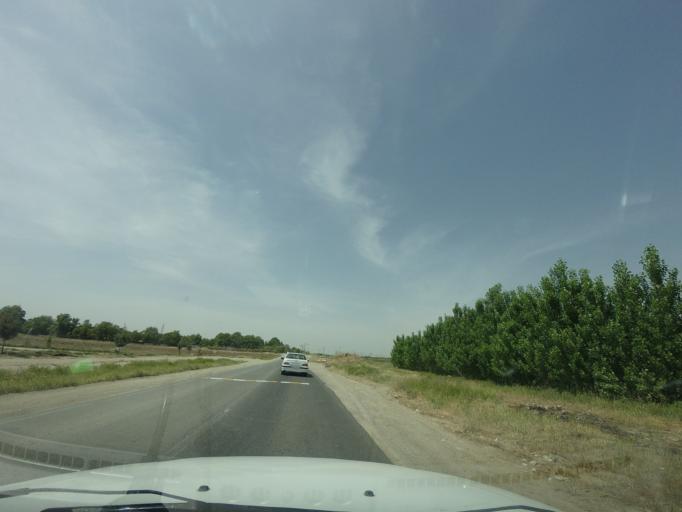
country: IR
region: Tehran
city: Eslamshahr
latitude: 35.6414
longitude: 51.2502
